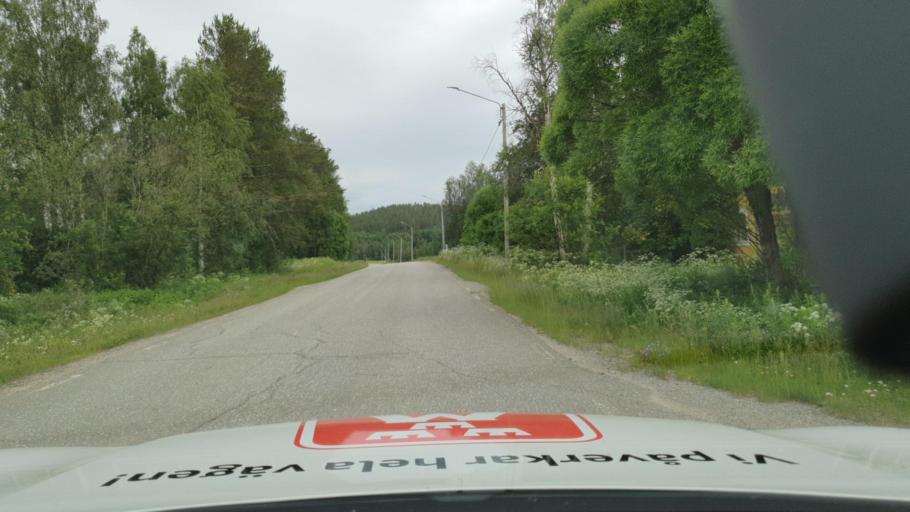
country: SE
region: Vaesterbotten
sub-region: Skelleftea Kommun
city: Burtraesk
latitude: 64.3068
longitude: 20.6527
